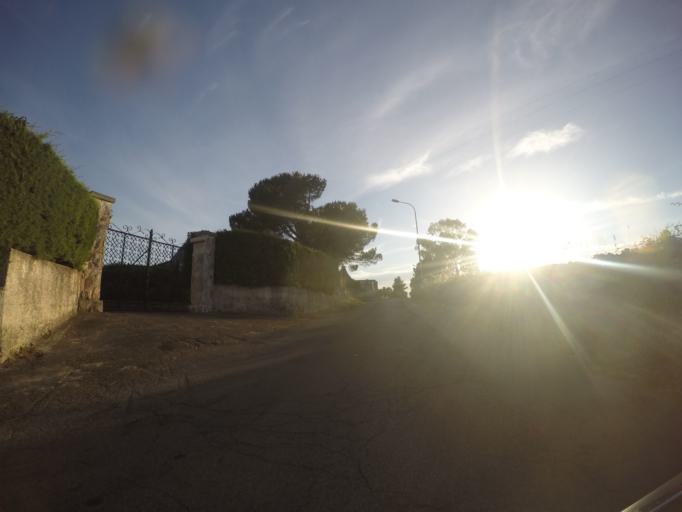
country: IT
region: Apulia
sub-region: Provincia di Taranto
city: Martina Franca
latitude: 40.6539
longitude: 17.3512
